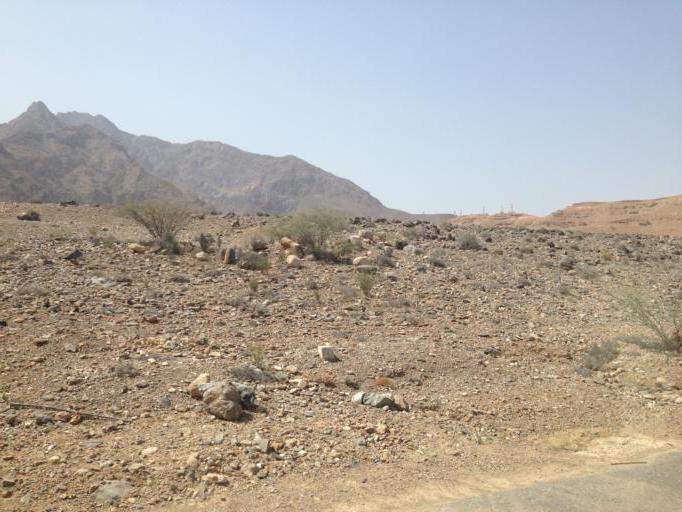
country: OM
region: Ash Sharqiyah
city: Ibra'
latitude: 23.0905
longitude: 58.8564
